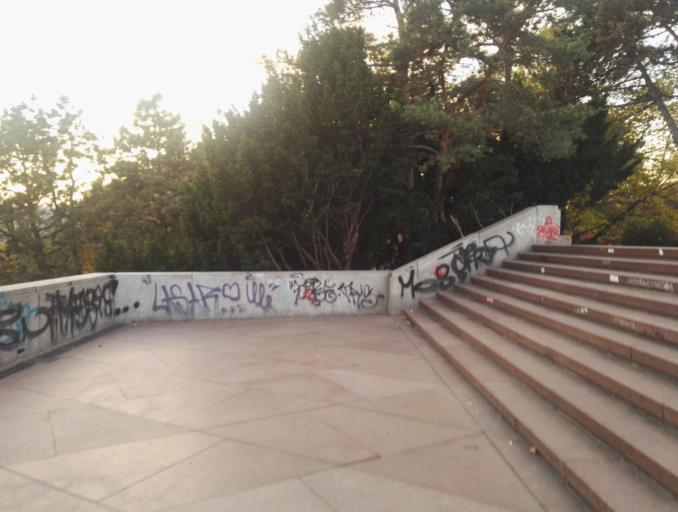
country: CZ
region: Praha
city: Prague
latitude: 50.0953
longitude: 14.4157
